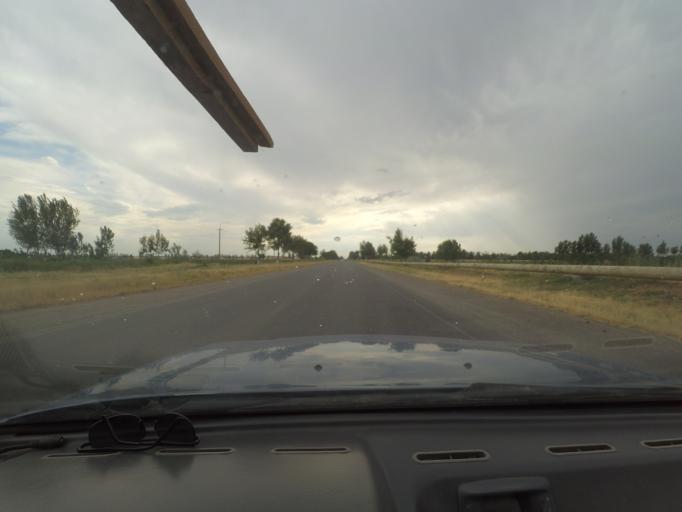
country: UZ
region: Sirdaryo
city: Guliston
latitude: 40.4922
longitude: 68.8332
